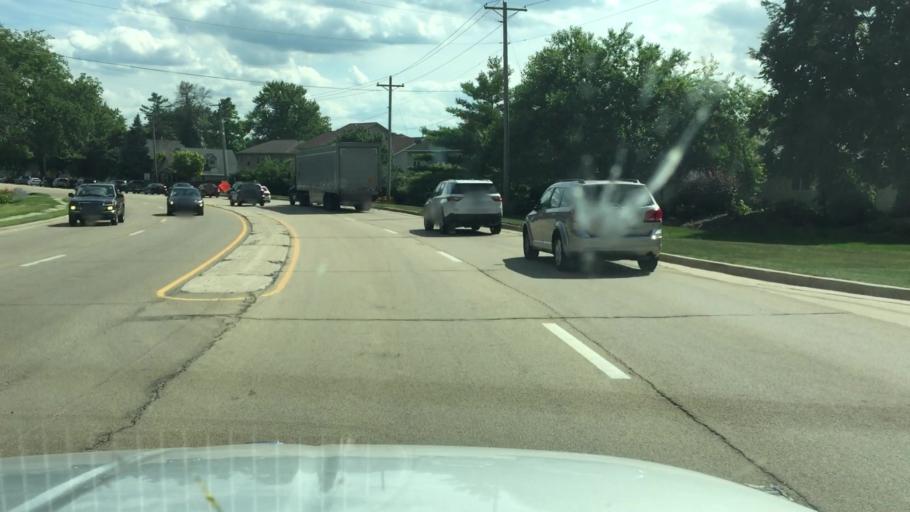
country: US
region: Illinois
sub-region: LaSalle County
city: Ottawa
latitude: 41.3623
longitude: -88.8407
